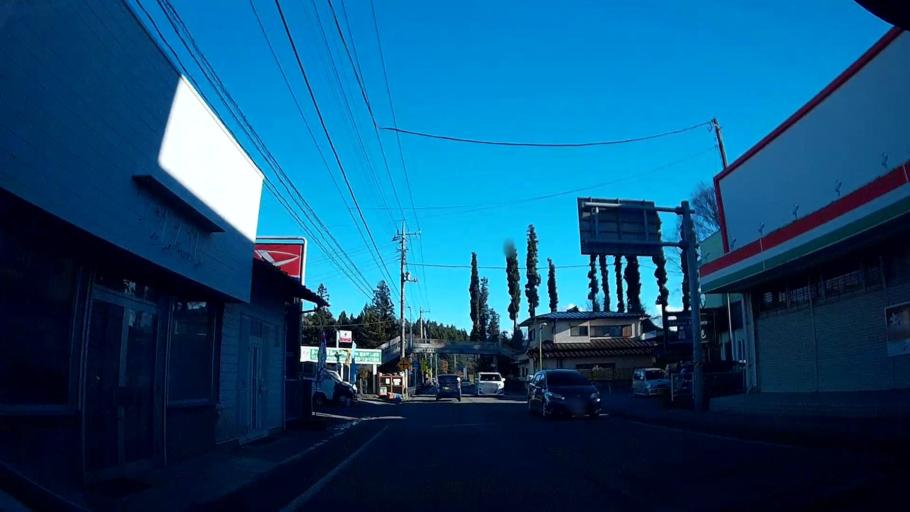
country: JP
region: Yamanashi
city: Fujikawaguchiko
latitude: 35.4710
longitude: 138.7985
